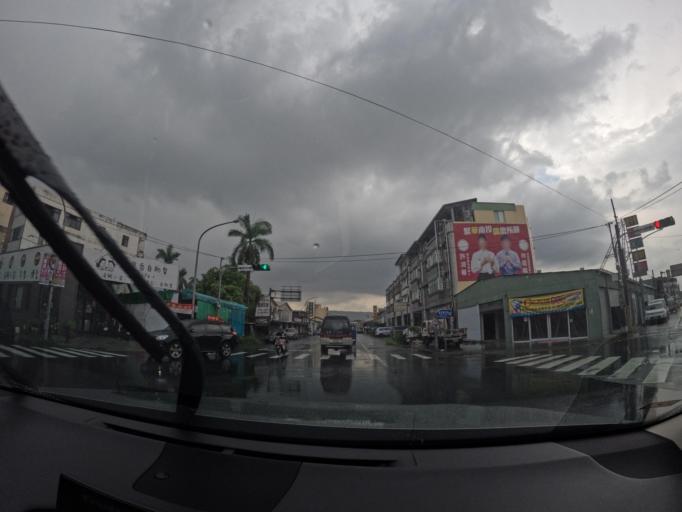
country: TW
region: Taiwan
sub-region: Nantou
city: Nantou
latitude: 23.9069
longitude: 120.6945
